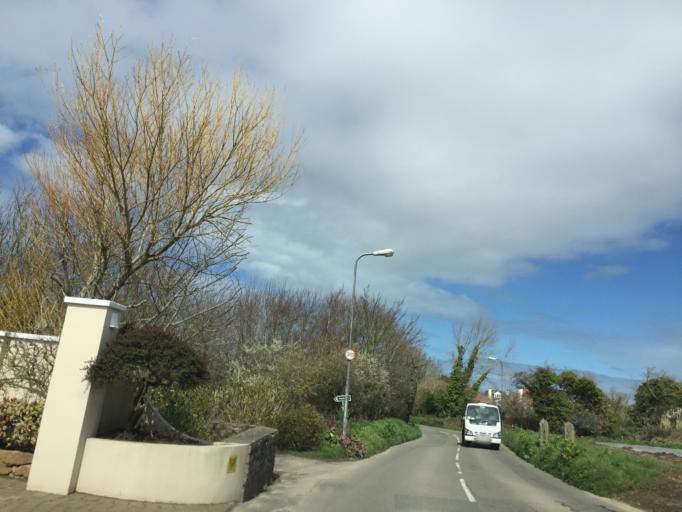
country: JE
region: St Helier
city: Saint Helier
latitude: 49.1814
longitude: -2.1769
